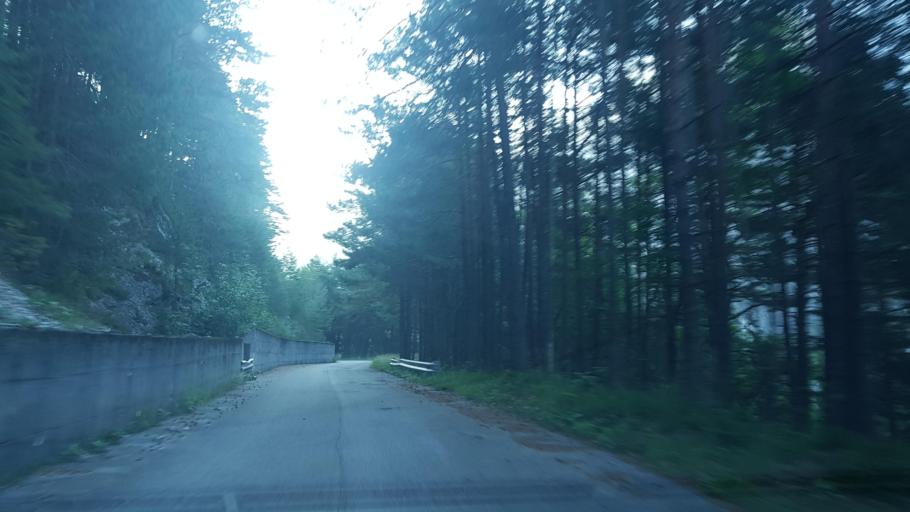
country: IT
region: Friuli Venezia Giulia
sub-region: Provincia di Udine
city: Malborghetto
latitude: 46.4558
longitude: 13.3953
